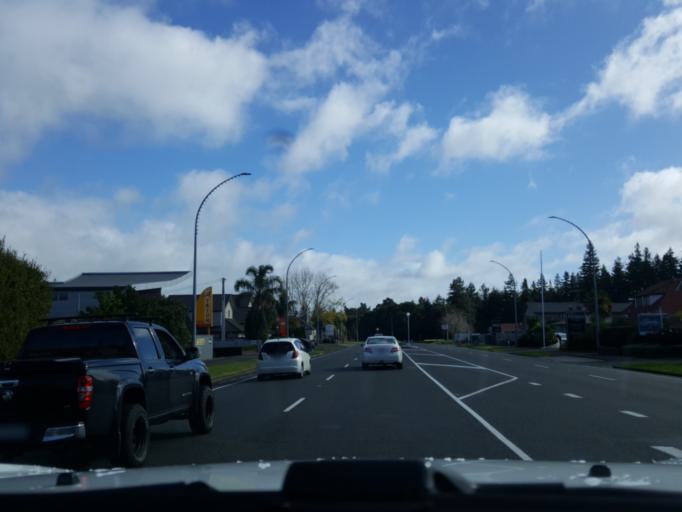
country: NZ
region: Waikato
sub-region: Hamilton City
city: Hamilton
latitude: -37.7767
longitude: 175.2679
